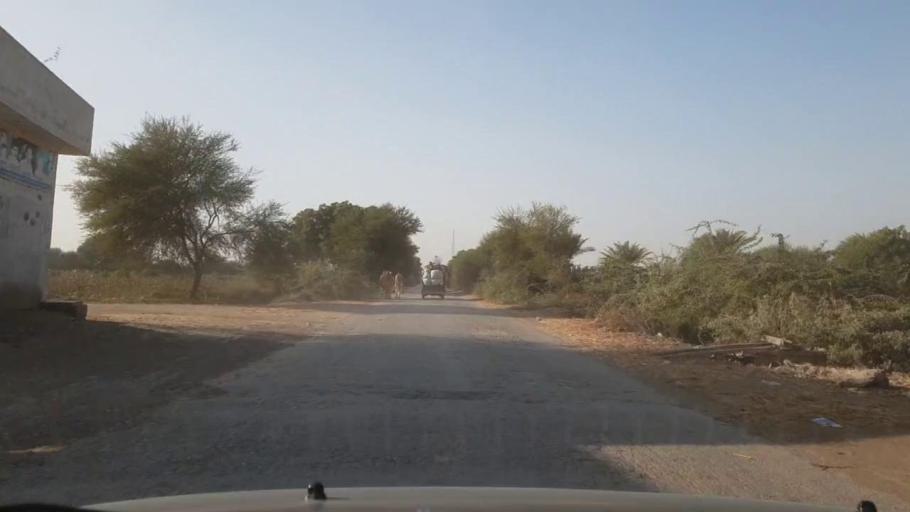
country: PK
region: Sindh
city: Chambar
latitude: 25.2083
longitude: 68.7844
